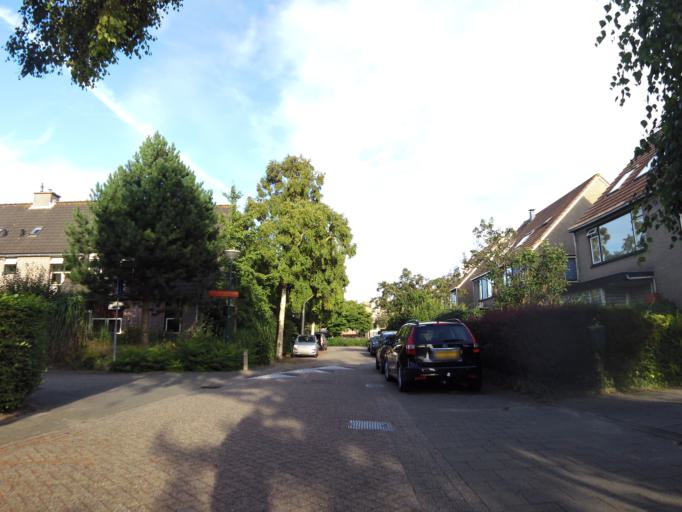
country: NL
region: South Holland
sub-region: Gemeente Oegstgeest
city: Oegstgeest
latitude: 52.1922
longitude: 4.4716
